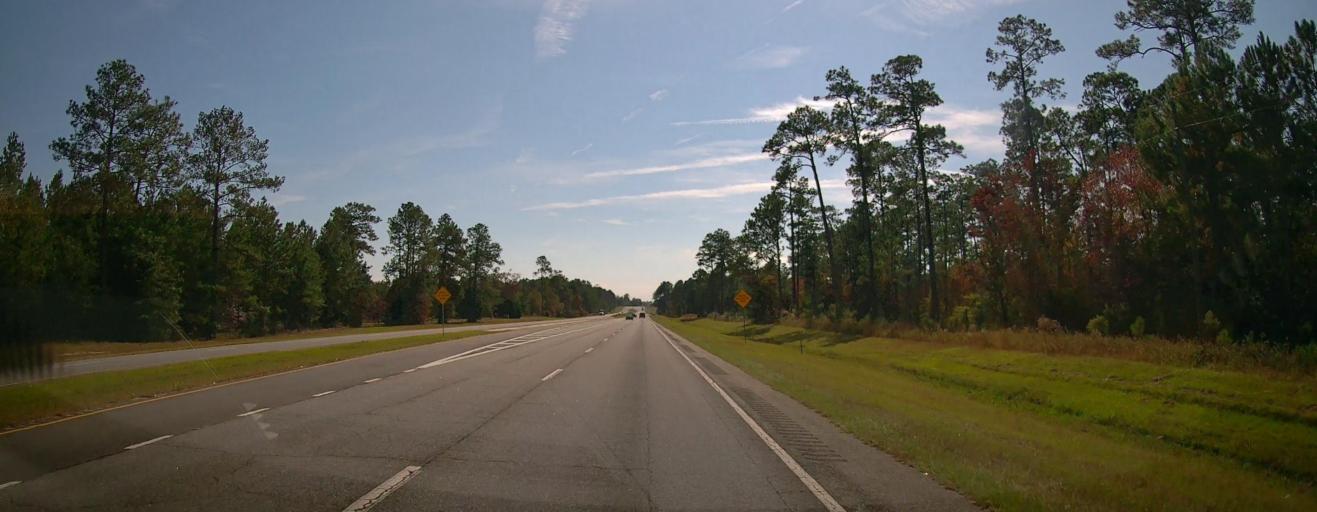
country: US
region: Georgia
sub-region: Lee County
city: Leesburg
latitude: 31.6724
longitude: -83.9960
